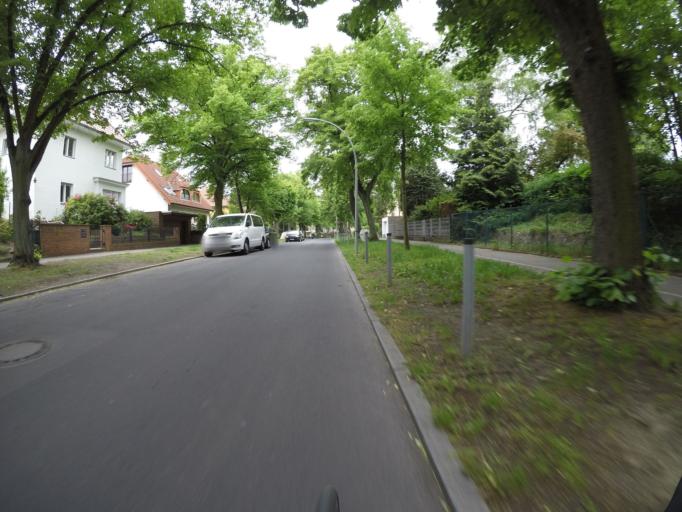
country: DE
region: Berlin
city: Hermsdorf
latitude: 52.6186
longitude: 13.3166
